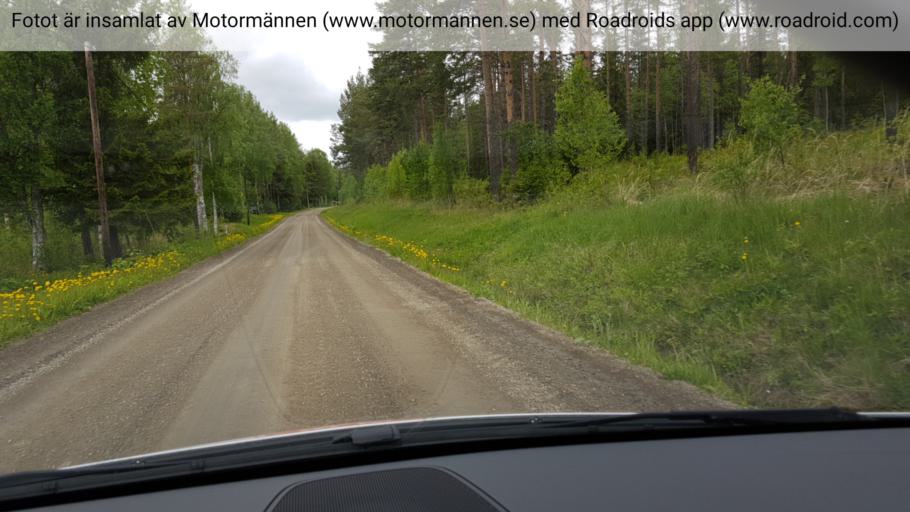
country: SE
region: Jaemtland
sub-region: Braecke Kommun
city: Braecke
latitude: 62.8682
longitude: 15.1765
